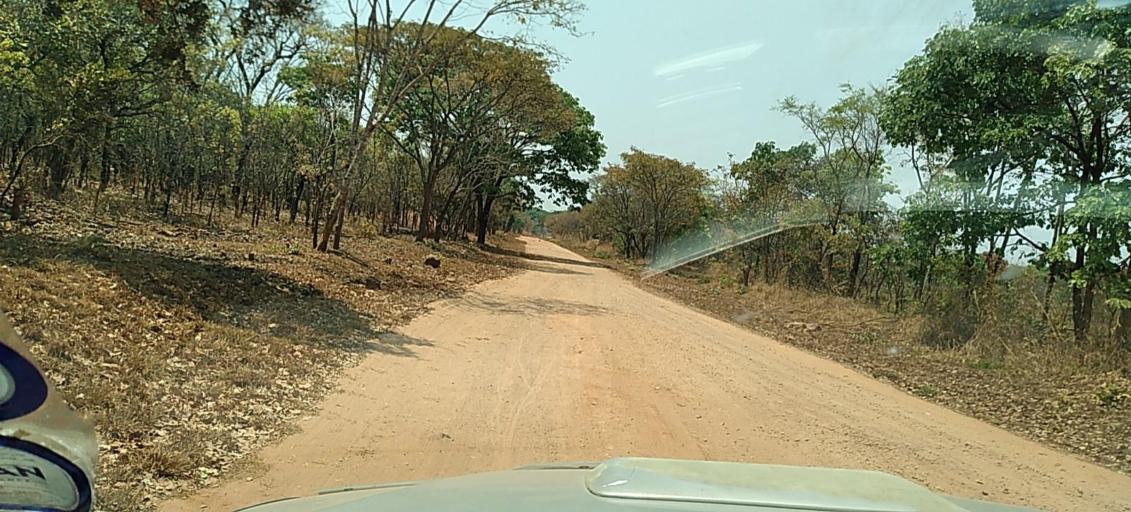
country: ZM
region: North-Western
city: Kasempa
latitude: -13.5508
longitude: 26.0163
